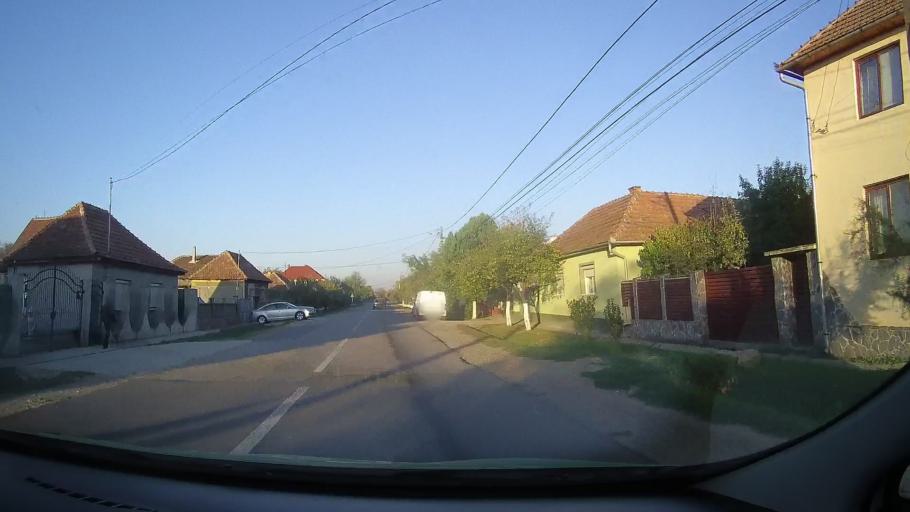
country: RO
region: Bihor
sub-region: Comuna Salard
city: Salard
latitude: 47.2182
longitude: 22.0340
